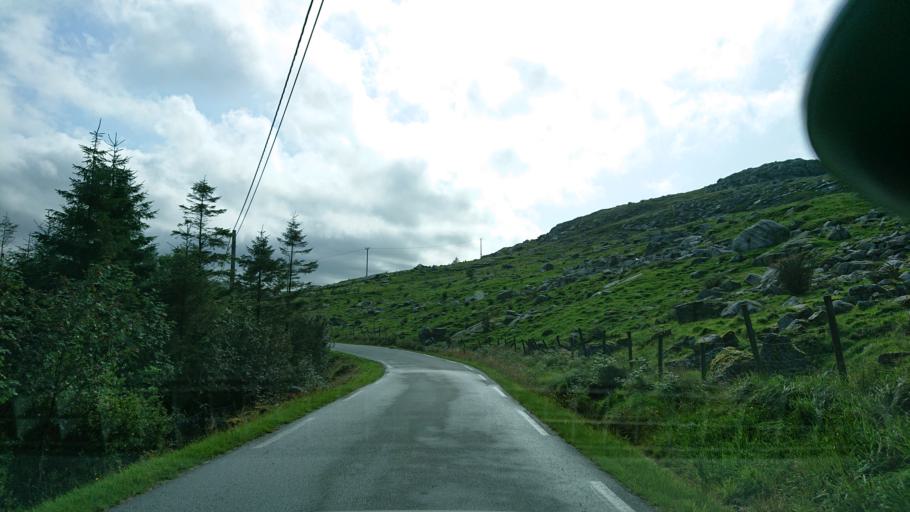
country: NO
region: Rogaland
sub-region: Gjesdal
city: Algard
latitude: 58.6990
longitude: 5.8894
